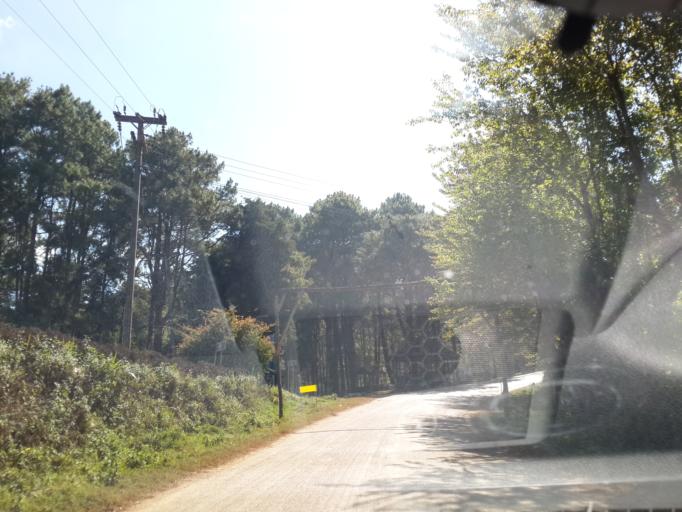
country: TH
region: Chiang Mai
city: Fang
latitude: 19.9315
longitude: 99.0428
